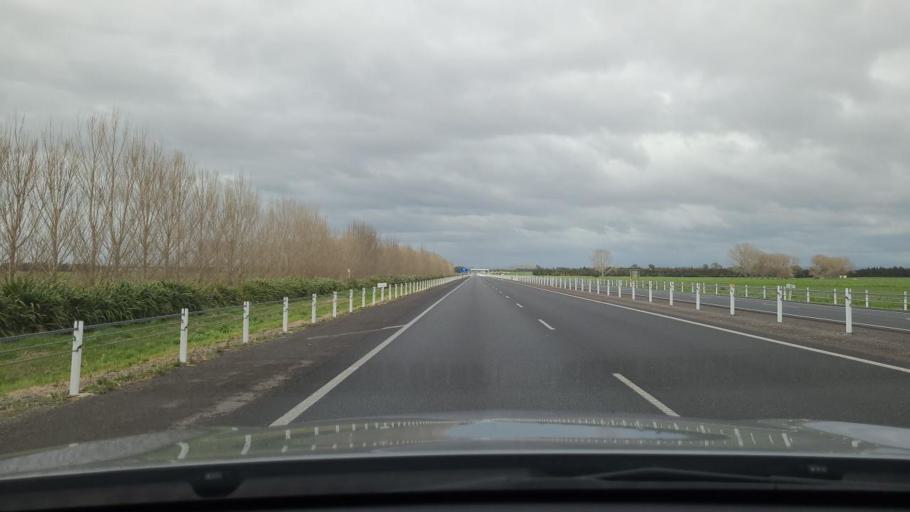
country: NZ
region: Bay of Plenty
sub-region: Western Bay of Plenty District
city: Maketu
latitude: -37.7664
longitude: 176.3739
